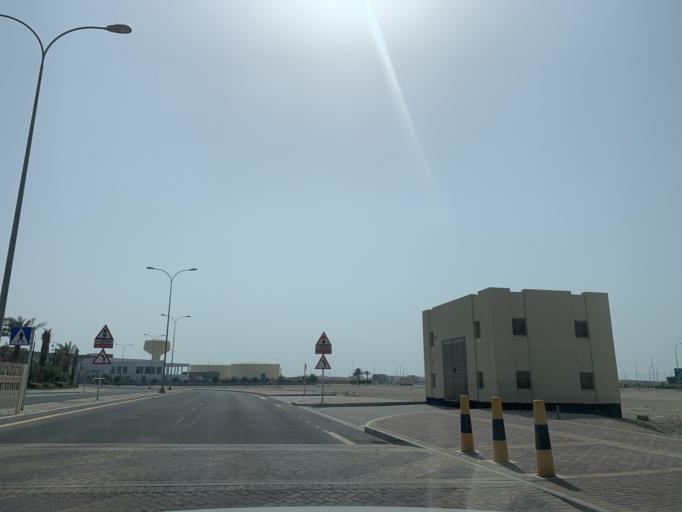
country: BH
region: Muharraq
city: Al Muharraq
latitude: 26.3064
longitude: 50.6379
